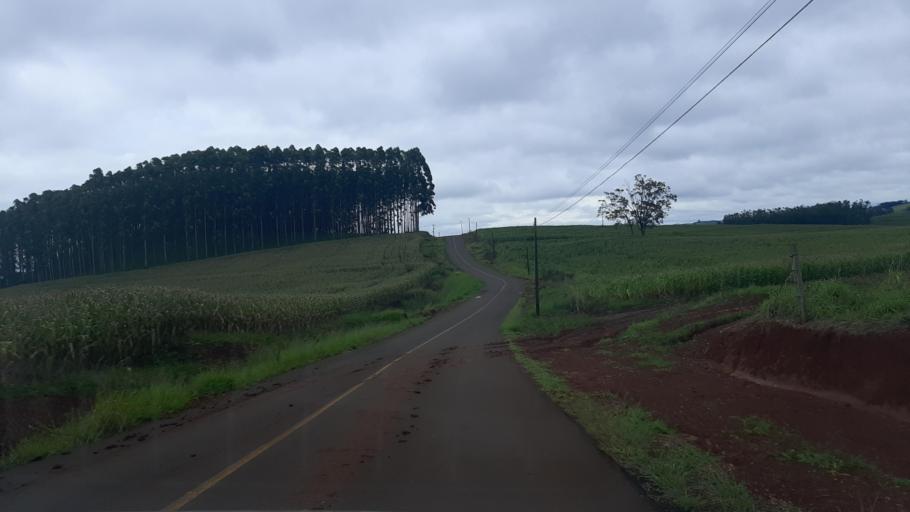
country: BR
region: Parana
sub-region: Ampere
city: Ampere
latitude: -26.0413
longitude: -53.4993
